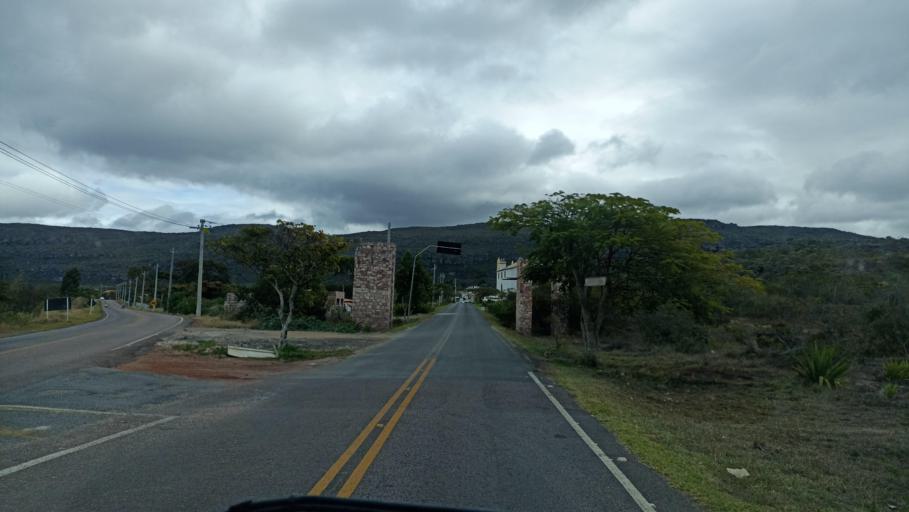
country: BR
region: Bahia
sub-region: Andarai
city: Vera Cruz
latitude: -13.0022
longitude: -41.3658
